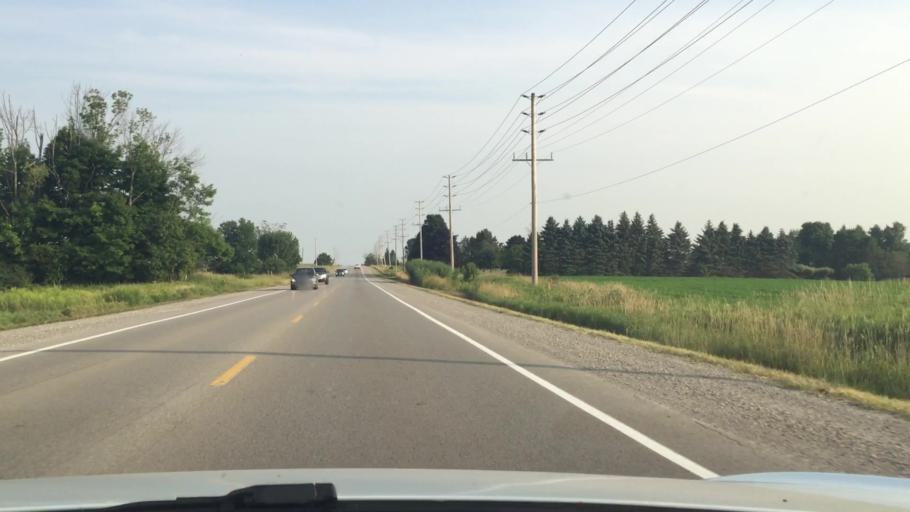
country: CA
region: Ontario
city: Oshawa
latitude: 43.8925
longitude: -78.7696
